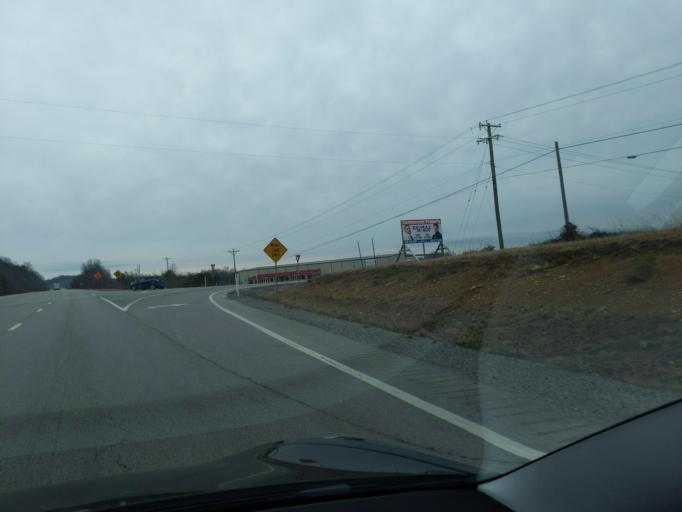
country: US
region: Kentucky
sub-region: Whitley County
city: Corbin
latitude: 36.9148
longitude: -84.0746
